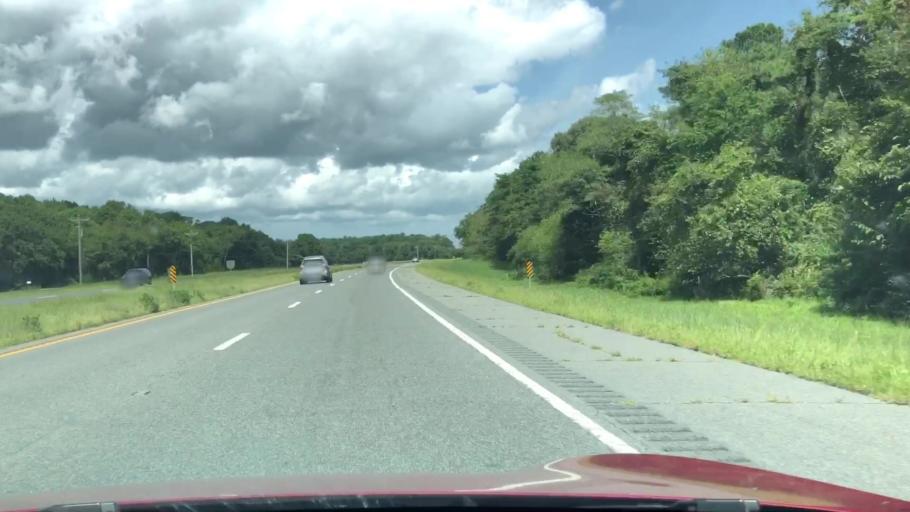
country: US
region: Virginia
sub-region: Northampton County
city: Cape Charles
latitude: 37.1477
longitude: -75.9707
